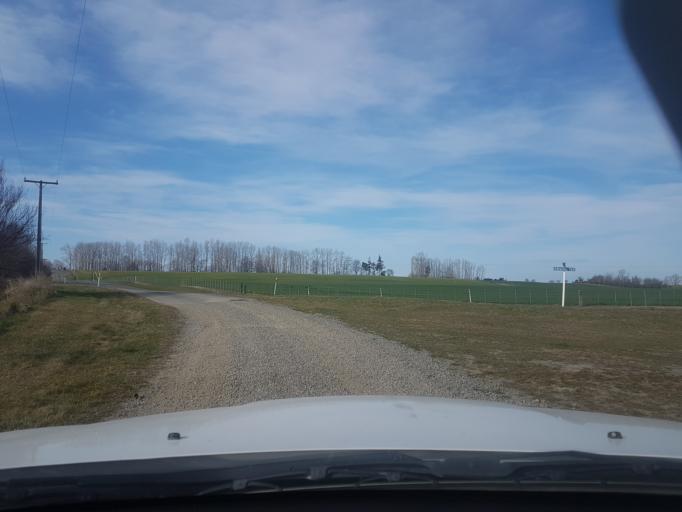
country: NZ
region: Canterbury
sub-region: Timaru District
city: Pleasant Point
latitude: -44.1295
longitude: 171.1813
